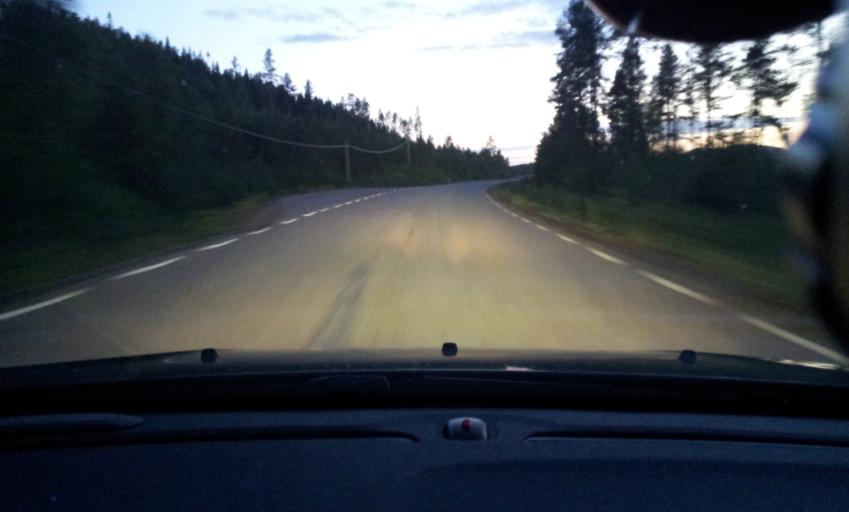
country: SE
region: Jaemtland
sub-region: Bergs Kommun
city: Hoverberg
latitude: 62.6543
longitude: 14.7996
